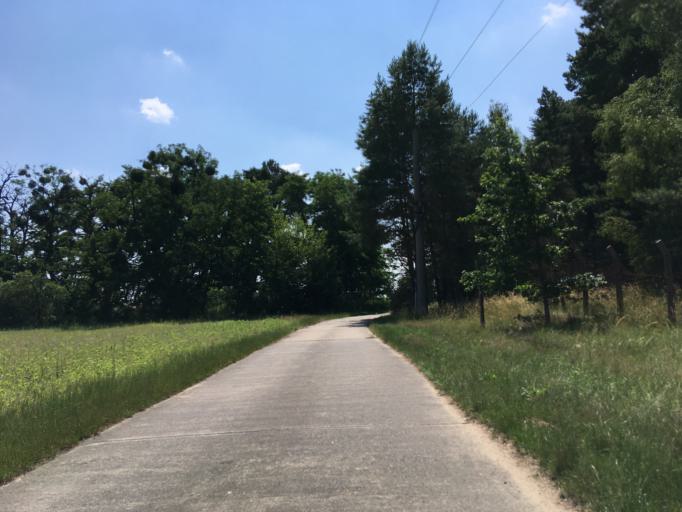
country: DE
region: Brandenburg
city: Werftpfuhl
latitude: 52.7108
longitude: 13.8237
